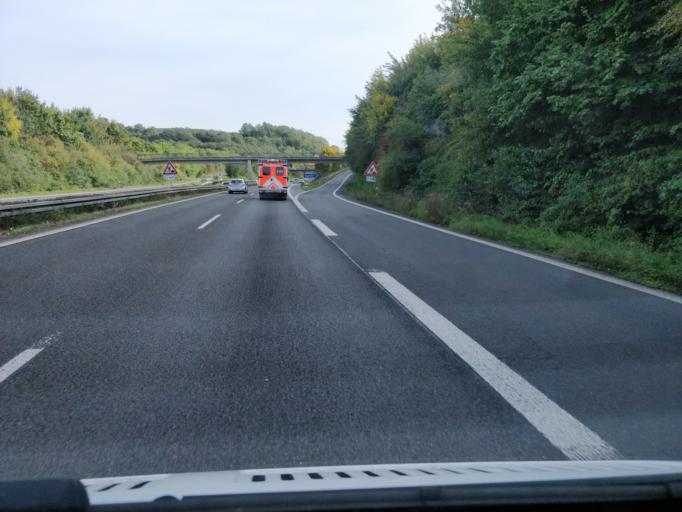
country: DE
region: North Rhine-Westphalia
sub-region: Regierungsbezirk Dusseldorf
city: Dinslaken
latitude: 51.5416
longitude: 6.7442
